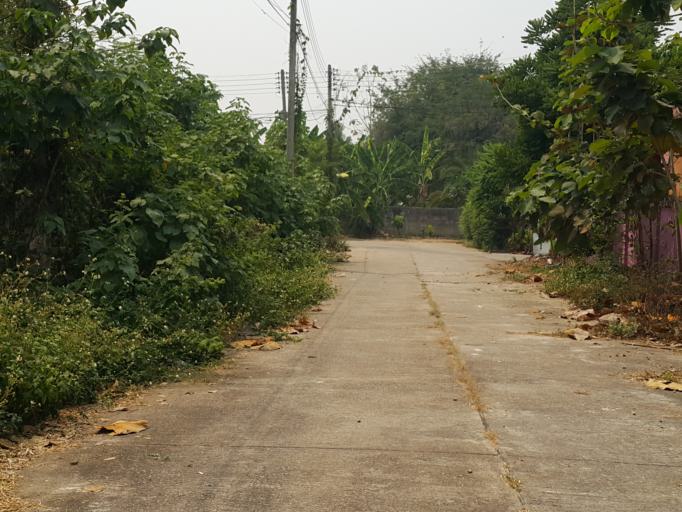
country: TH
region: Chiang Mai
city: Saraphi
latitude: 18.7399
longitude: 99.0194
